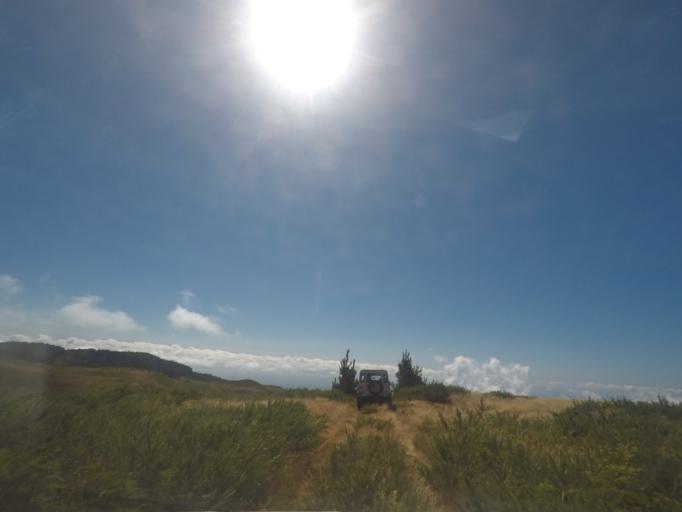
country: PT
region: Madeira
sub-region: Funchal
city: Nossa Senhora do Monte
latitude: 32.7103
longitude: -16.9069
